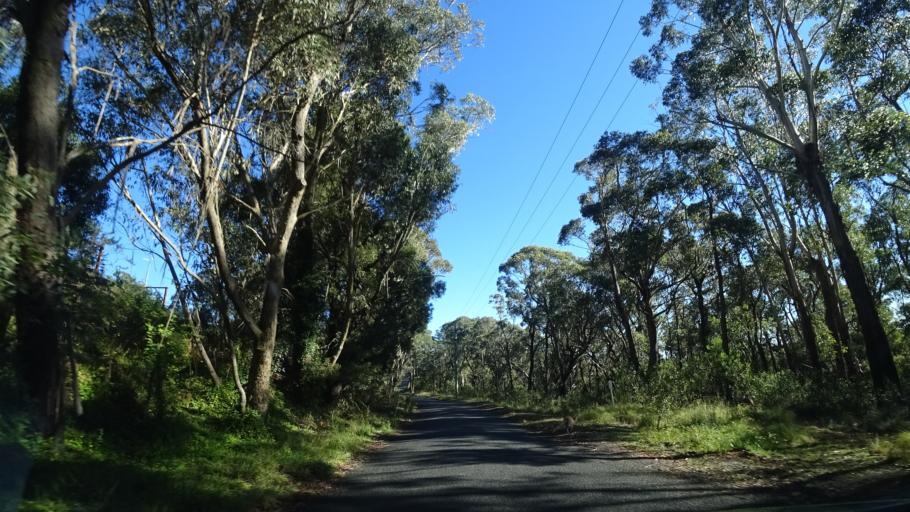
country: AU
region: New South Wales
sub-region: Blue Mountains Municipality
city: Blackheath
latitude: -33.5101
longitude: 150.2820
